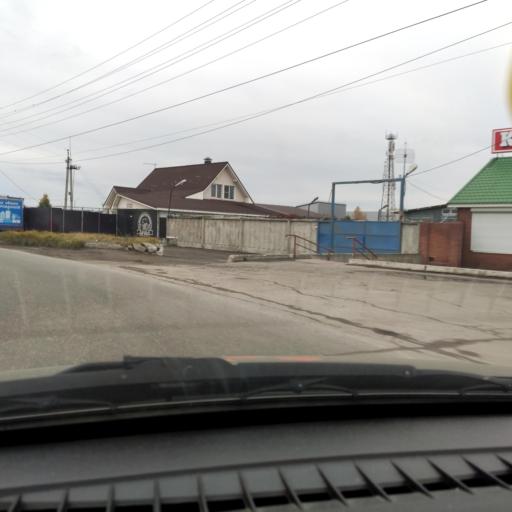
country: RU
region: Samara
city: Podstepki
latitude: 53.5235
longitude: 49.1960
